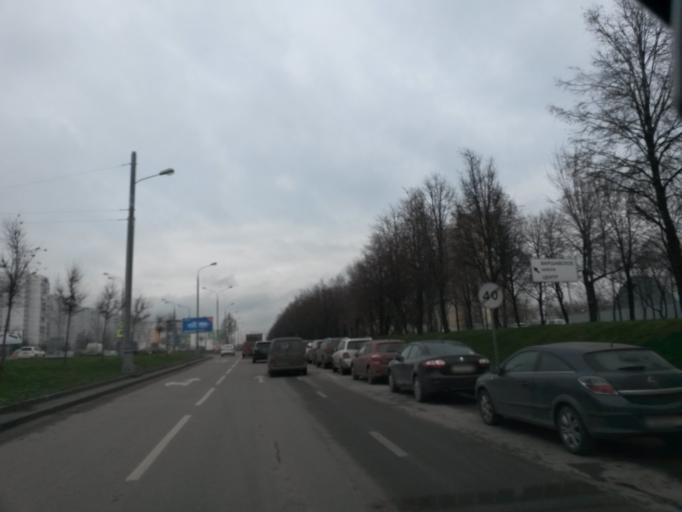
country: RU
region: Moscow
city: Nagornyy
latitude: 55.6228
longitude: 37.6157
